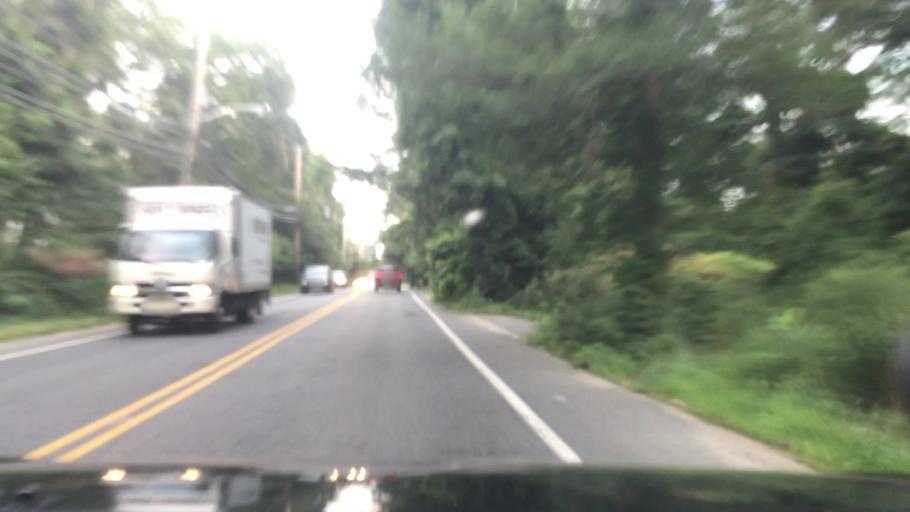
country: US
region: New Jersey
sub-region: Ocean County
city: Lakewood
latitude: 40.0820
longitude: -74.2573
